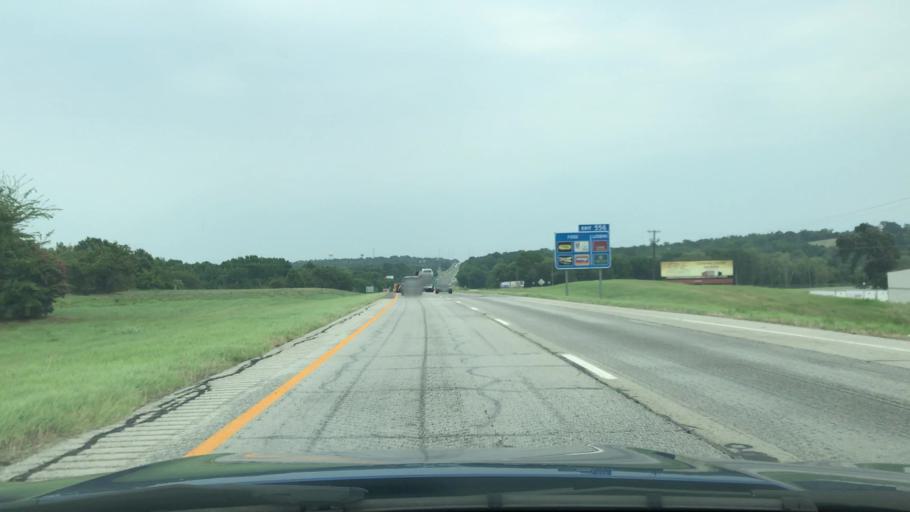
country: US
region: Texas
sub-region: Smith County
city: Lindale
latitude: 32.4682
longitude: -95.4095
